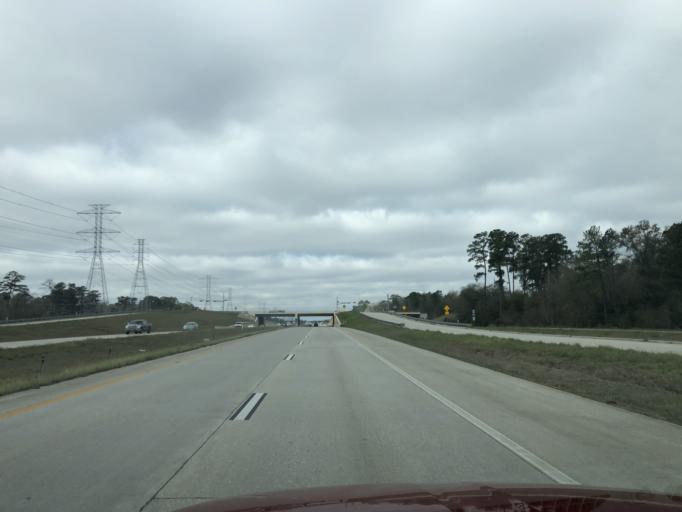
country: US
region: Texas
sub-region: Harris County
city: Spring
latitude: 30.0886
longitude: -95.4544
